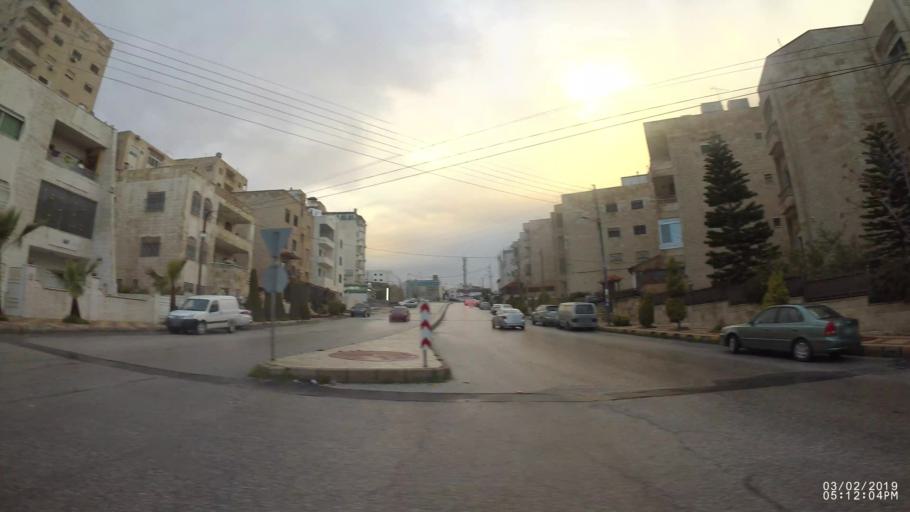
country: JO
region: Amman
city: Amman
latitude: 31.9905
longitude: 35.9145
